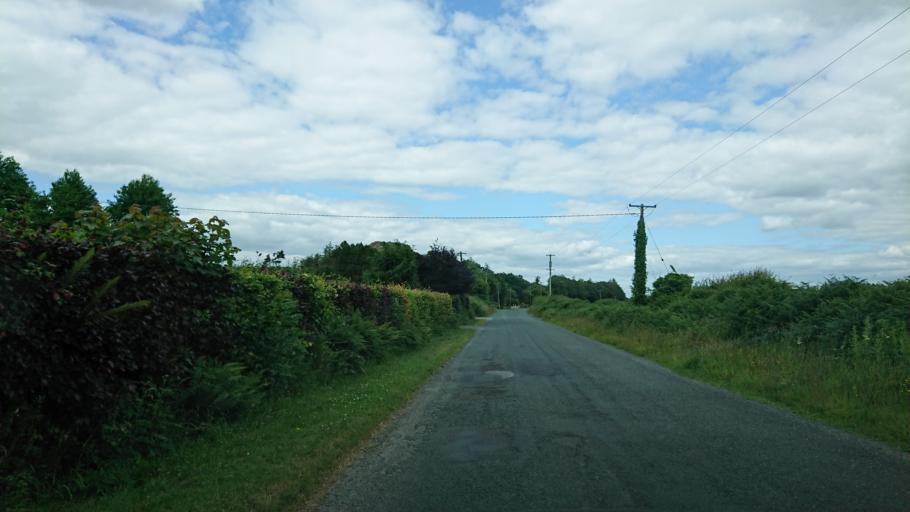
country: IE
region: Munster
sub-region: Waterford
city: Tra Mhor
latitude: 52.2074
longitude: -7.1750
